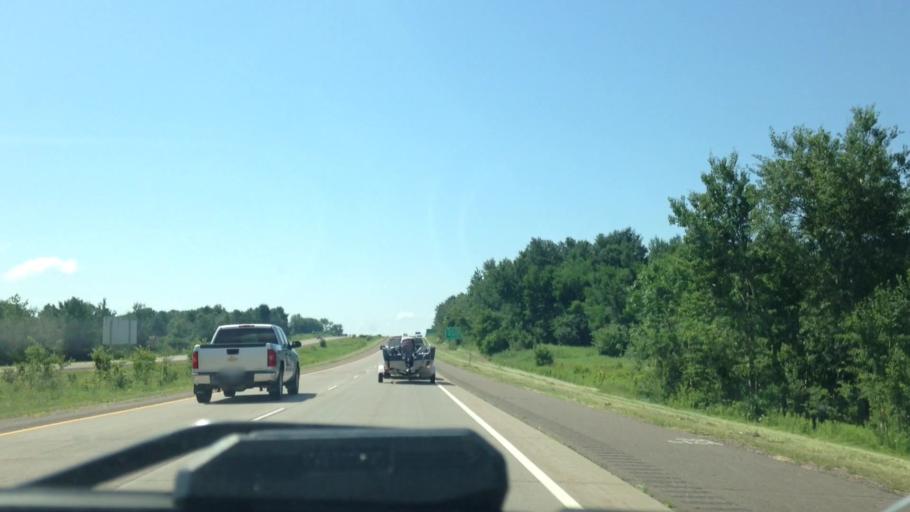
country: US
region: Wisconsin
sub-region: Barron County
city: Rice Lake
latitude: 45.4931
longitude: -91.7638
